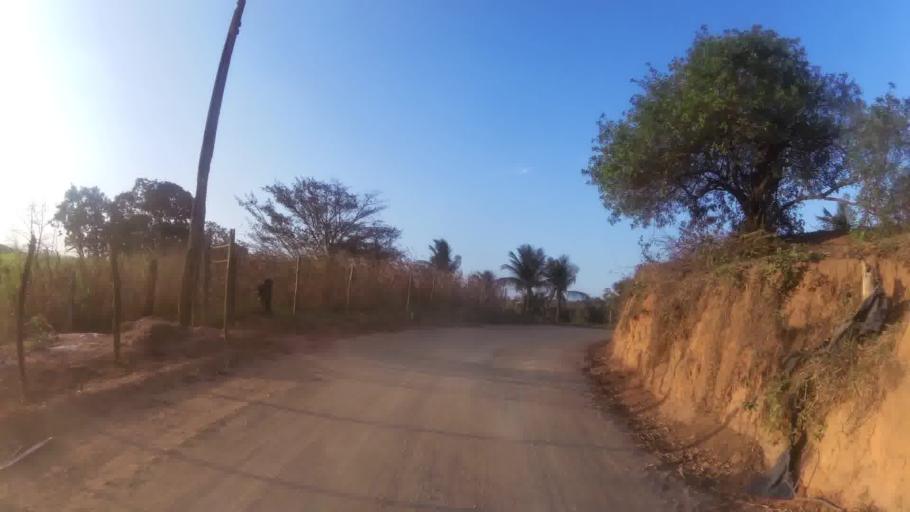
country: BR
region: Espirito Santo
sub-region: Piuma
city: Piuma
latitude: -20.8909
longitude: -40.8025
